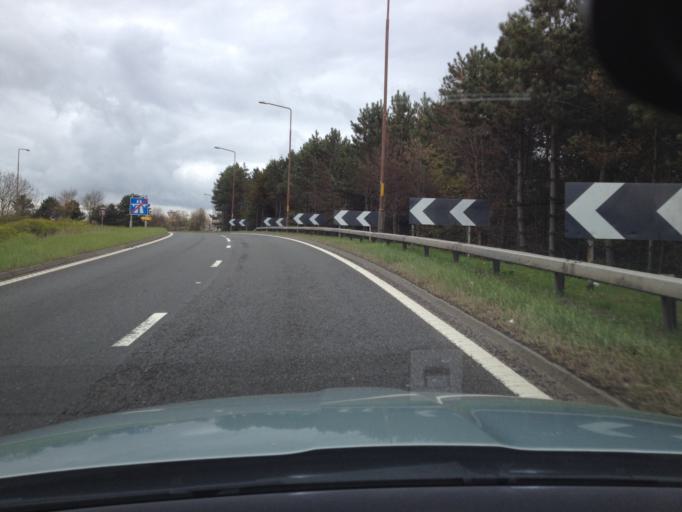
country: GB
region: Scotland
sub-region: West Lothian
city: Blackburn
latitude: 55.8963
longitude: -3.5953
